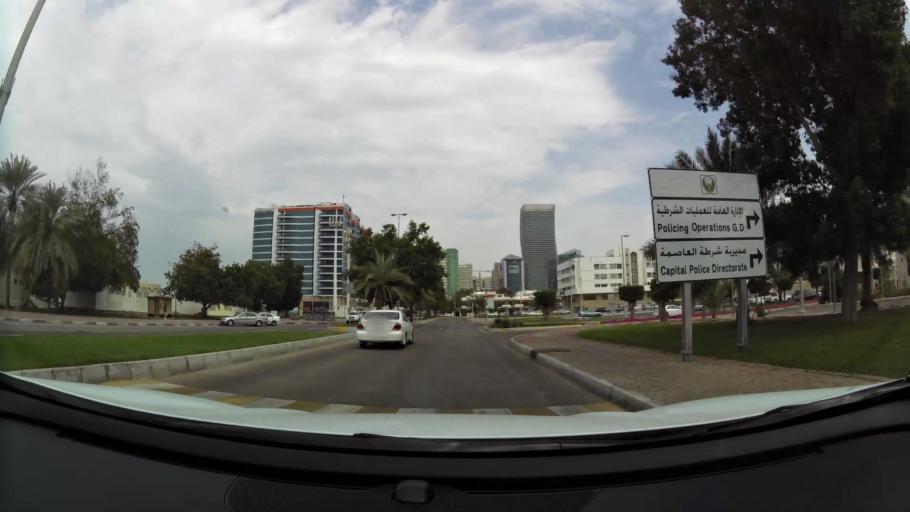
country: AE
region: Abu Dhabi
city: Abu Dhabi
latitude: 24.4653
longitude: 54.3328
